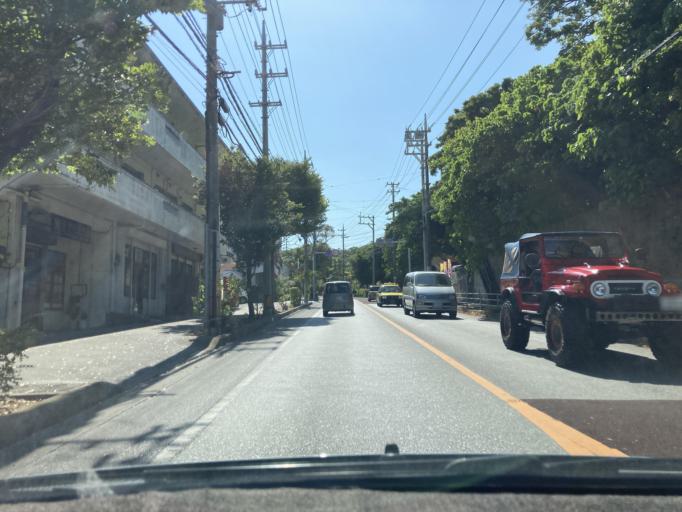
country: JP
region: Okinawa
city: Ginowan
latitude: 26.2598
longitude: 127.7229
